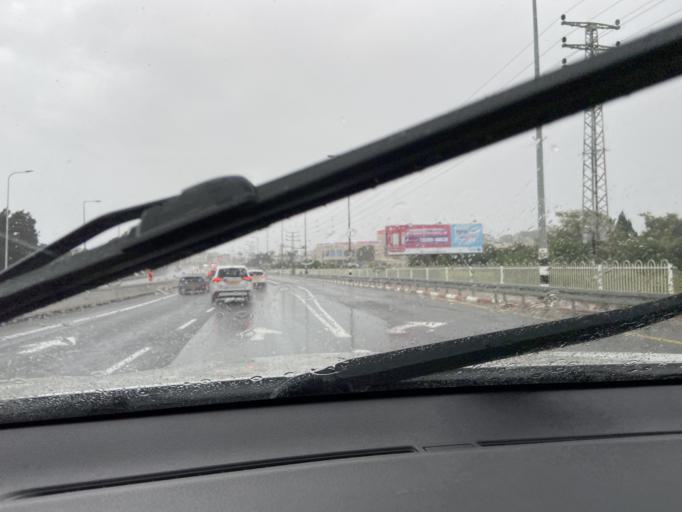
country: IL
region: Northern District
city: El Mazra`a
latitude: 32.9842
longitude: 35.0951
